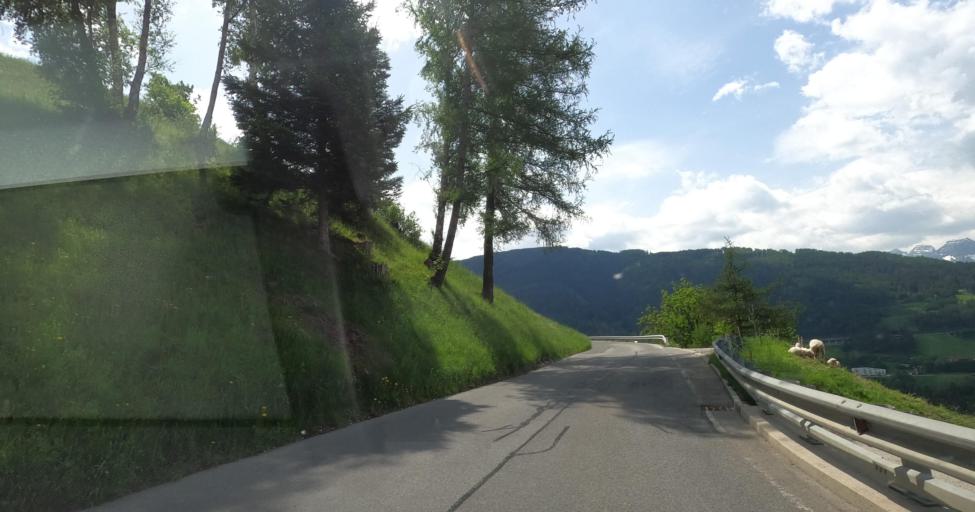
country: AT
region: Tyrol
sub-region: Politischer Bezirk Innsbruck Land
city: Schoenberg im Stubaital
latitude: 47.1830
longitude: 11.4344
